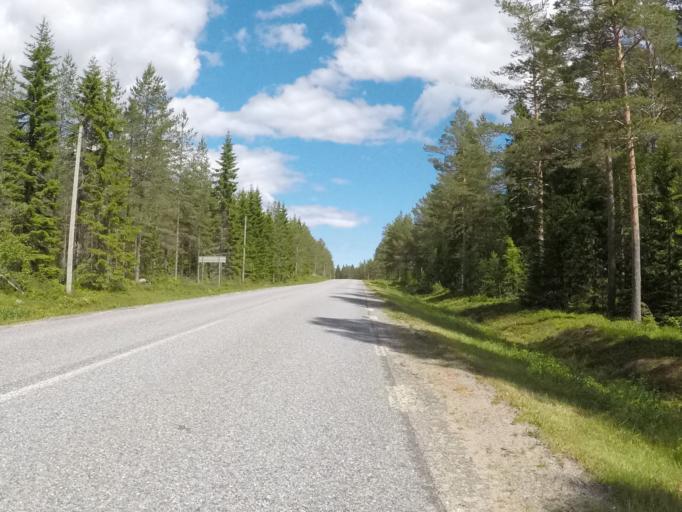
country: SE
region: Vaesterbotten
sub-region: Robertsfors Kommun
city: Robertsfors
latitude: 63.9564
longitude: 20.8013
